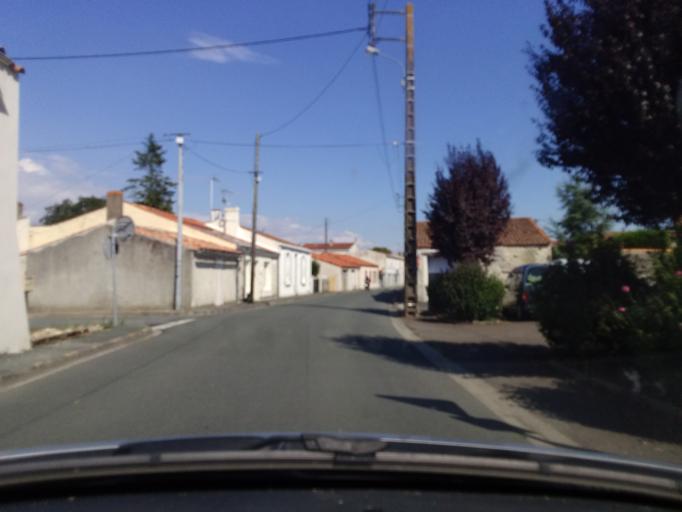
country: FR
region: Pays de la Loire
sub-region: Departement de la Vendee
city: Triaize
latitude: 46.3942
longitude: -1.1982
